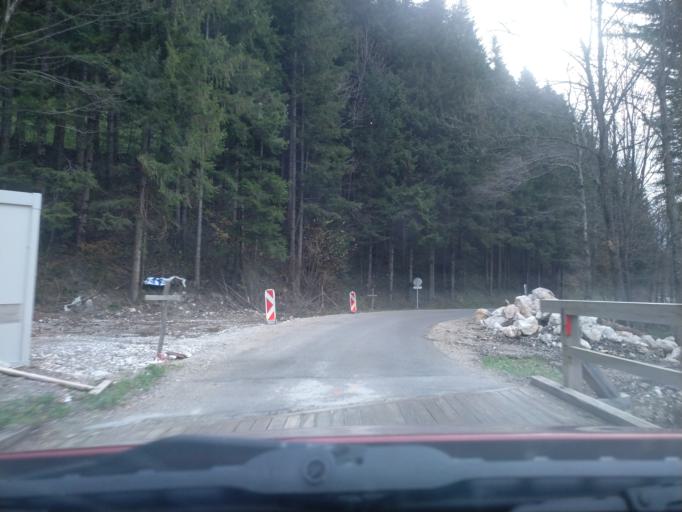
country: SI
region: Luce
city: Luce
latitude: 46.3185
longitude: 14.7042
